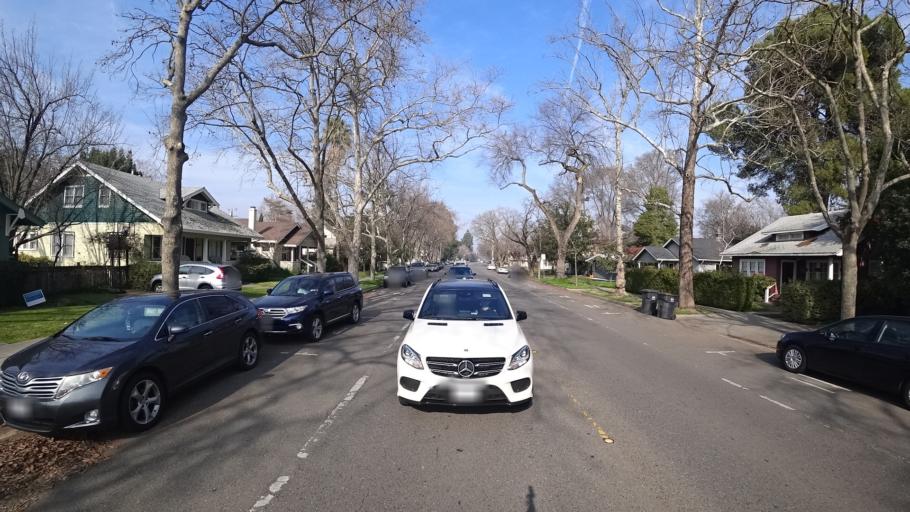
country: US
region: California
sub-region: Yolo County
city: Davis
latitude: 38.5490
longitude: -121.7416
